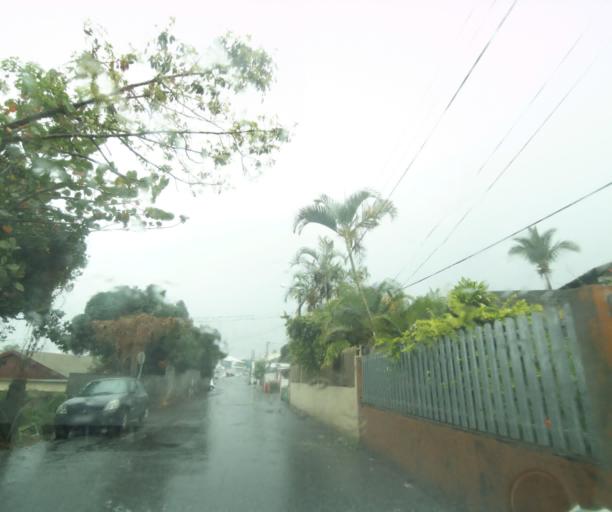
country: RE
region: Reunion
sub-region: Reunion
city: La Possession
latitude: -20.9842
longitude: 55.3261
